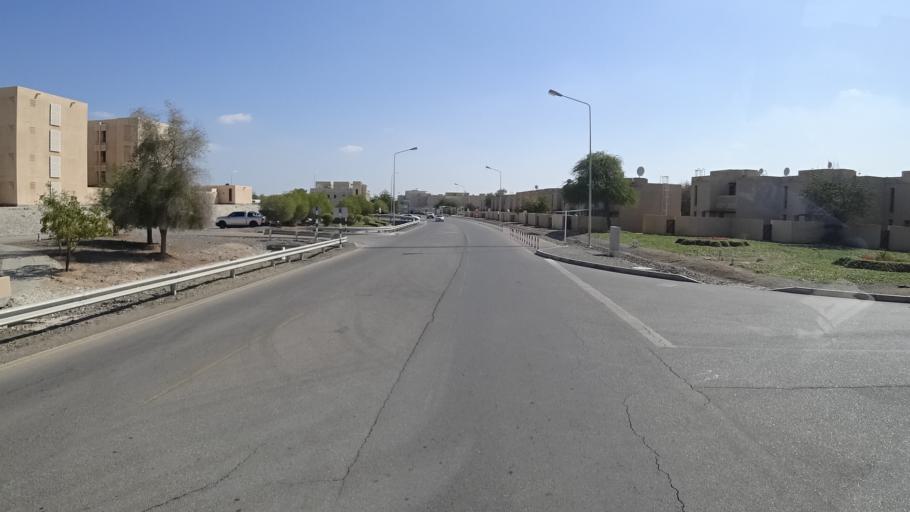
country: OM
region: Muhafazat Masqat
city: As Sib al Jadidah
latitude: 23.5860
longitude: 58.1669
